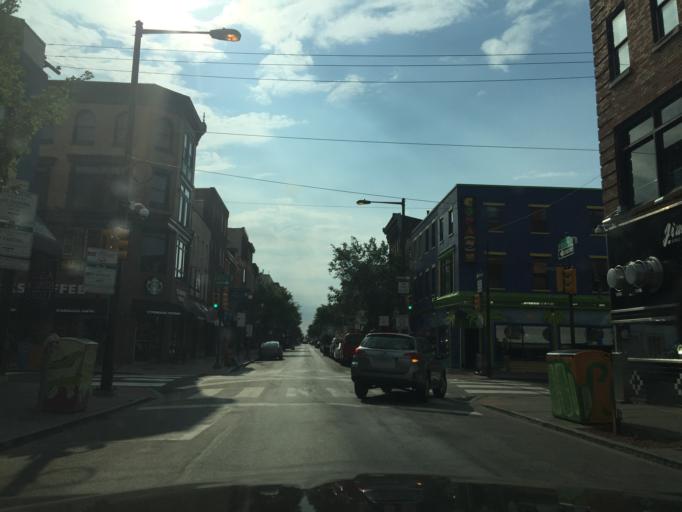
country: US
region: Pennsylvania
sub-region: Philadelphia County
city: Philadelphia
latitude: 39.9417
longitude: -75.1495
